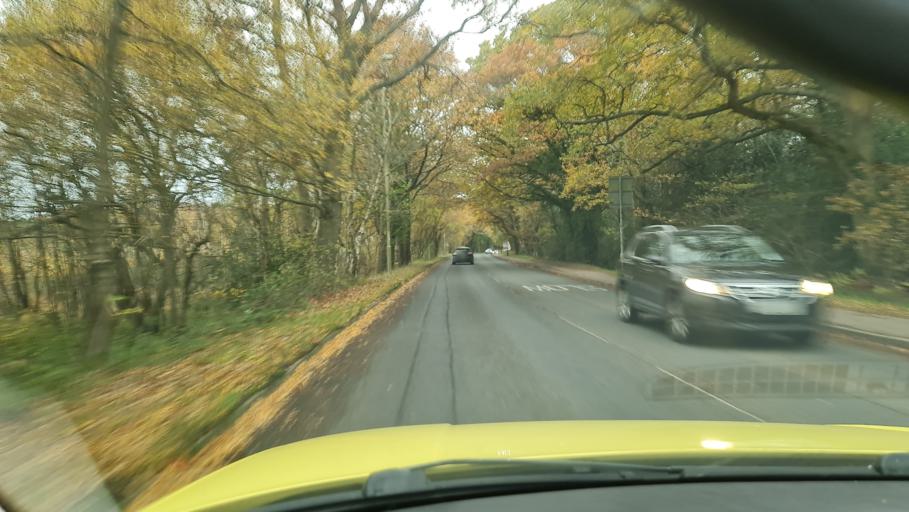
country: GB
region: England
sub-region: Bracknell Forest
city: Sandhurst
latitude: 51.3318
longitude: -0.7979
